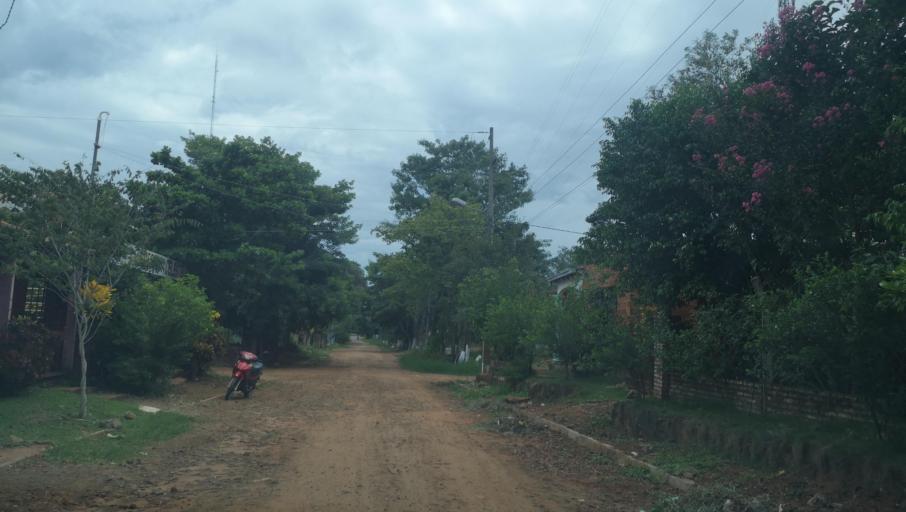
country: PY
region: San Pedro
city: Capiibary
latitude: -24.7278
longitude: -56.0144
